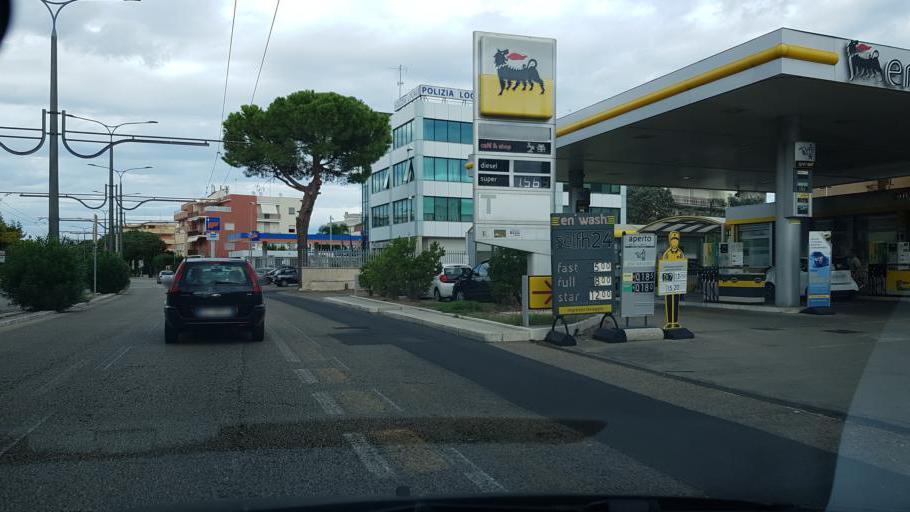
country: IT
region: Apulia
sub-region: Provincia di Lecce
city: Lecce
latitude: 40.3490
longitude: 18.1854
